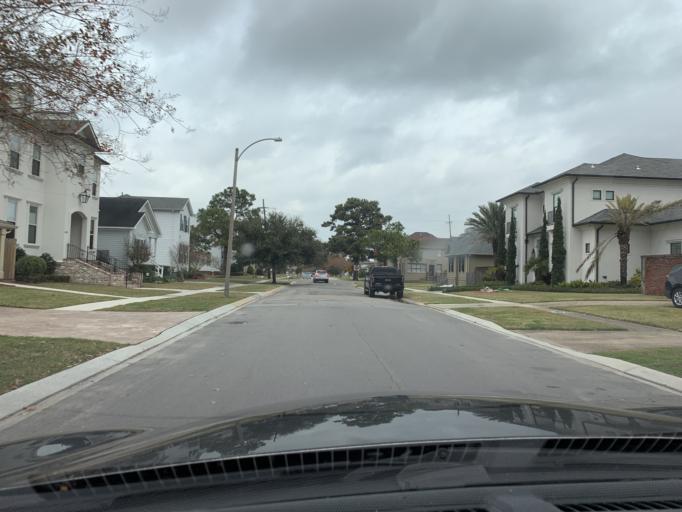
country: US
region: Louisiana
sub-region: Jefferson Parish
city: Metairie
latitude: 30.0057
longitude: -90.1036
